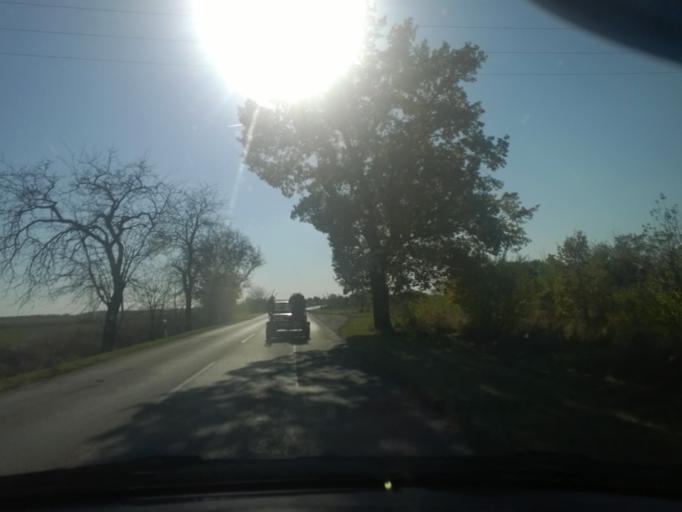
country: HU
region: Csongrad
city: Szegvar
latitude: 46.5476
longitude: 20.3170
